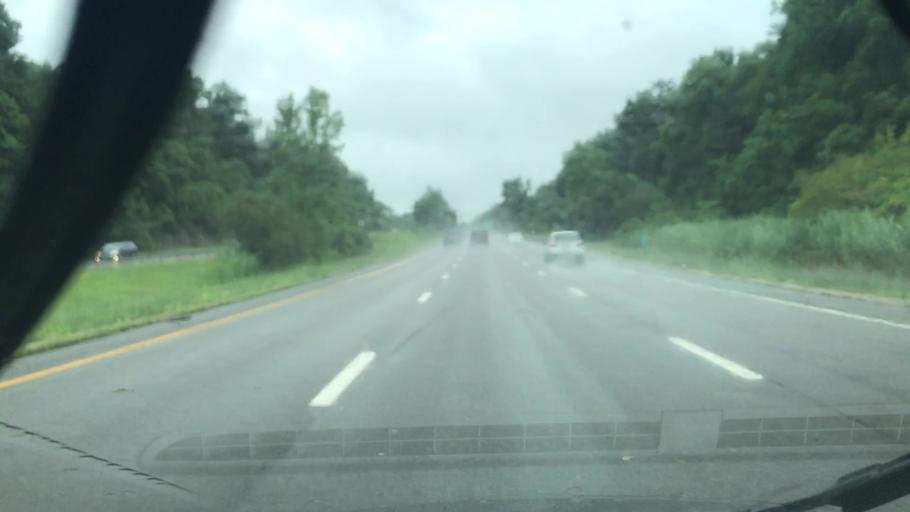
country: US
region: New York
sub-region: Westchester County
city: Briarcliff Manor
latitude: 41.1759
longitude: -73.8102
